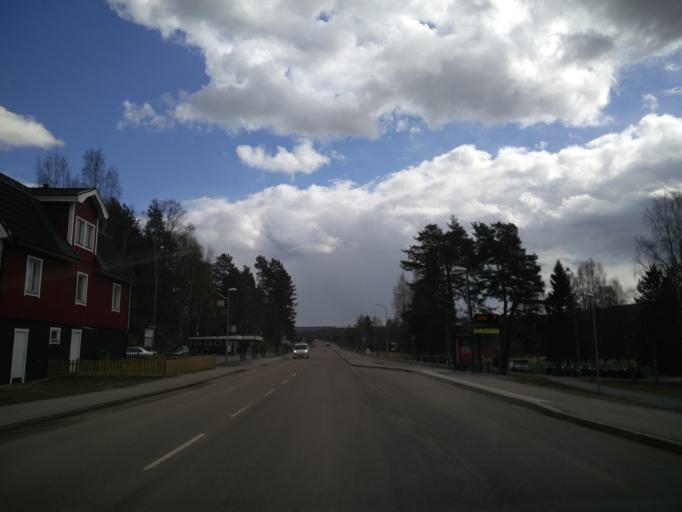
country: SE
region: Vaesternorrland
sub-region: Sundsvalls Kommun
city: Sundsvall
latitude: 62.4151
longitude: 17.2157
